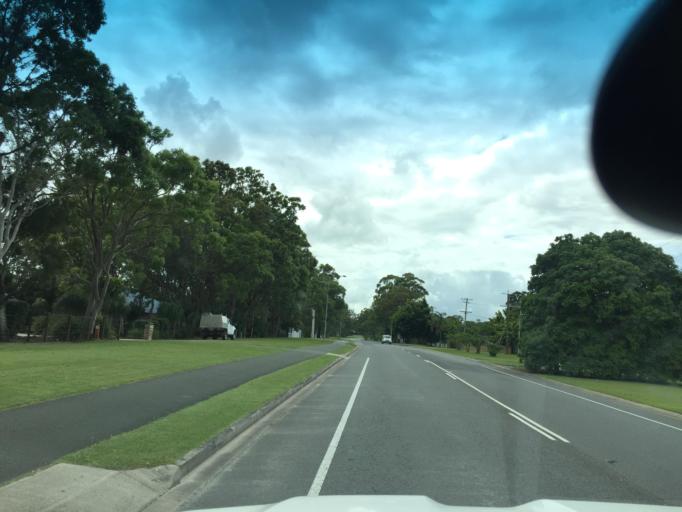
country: AU
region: Queensland
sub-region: Moreton Bay
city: Burpengary
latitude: -27.1317
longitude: 152.9846
